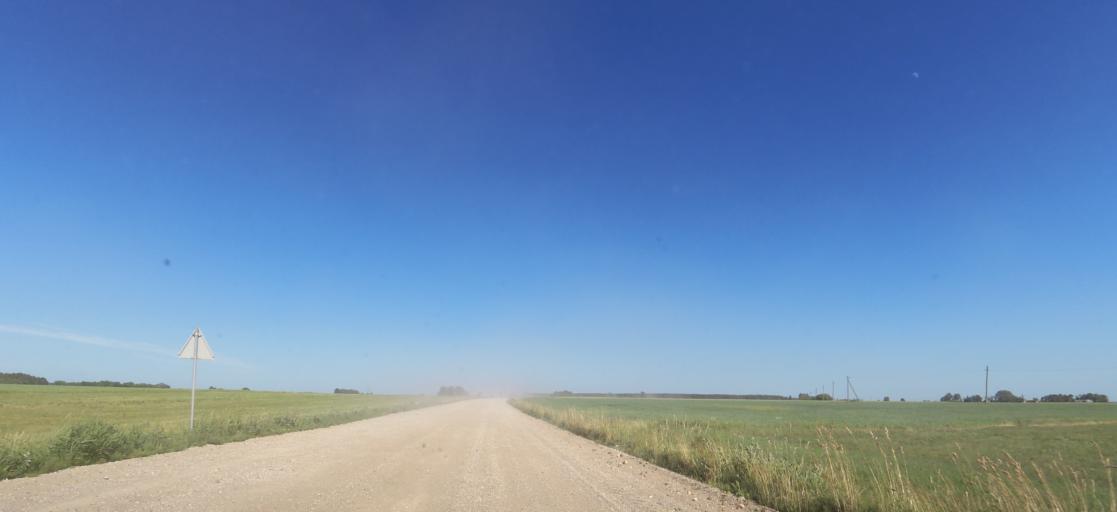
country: LT
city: Vabalninkas
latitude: 56.0264
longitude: 24.6795
